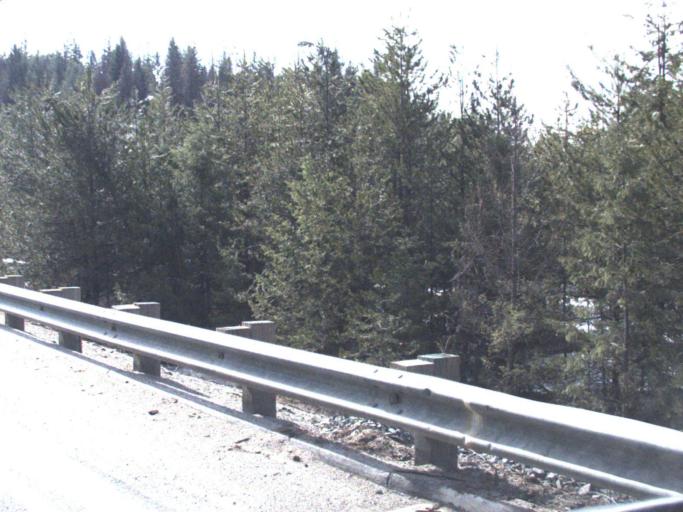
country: US
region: Washington
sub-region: Stevens County
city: Colville
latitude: 48.5105
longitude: -117.6774
